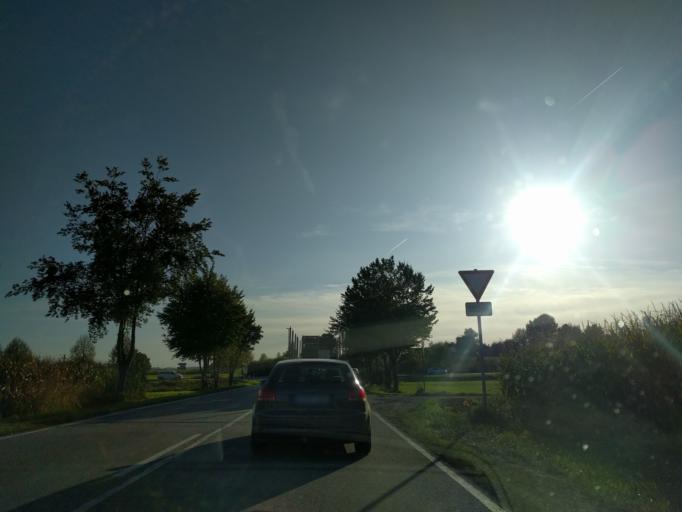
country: DE
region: Bavaria
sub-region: Lower Bavaria
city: Osterhofen
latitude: 48.6911
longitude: 13.0388
